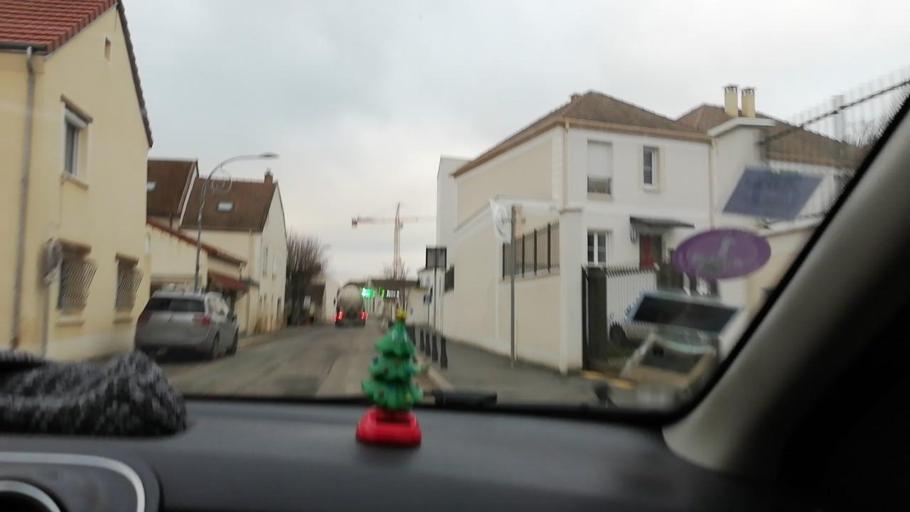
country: FR
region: Ile-de-France
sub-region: Departement de Seine-et-Marne
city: Charny
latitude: 48.9704
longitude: 2.7608
